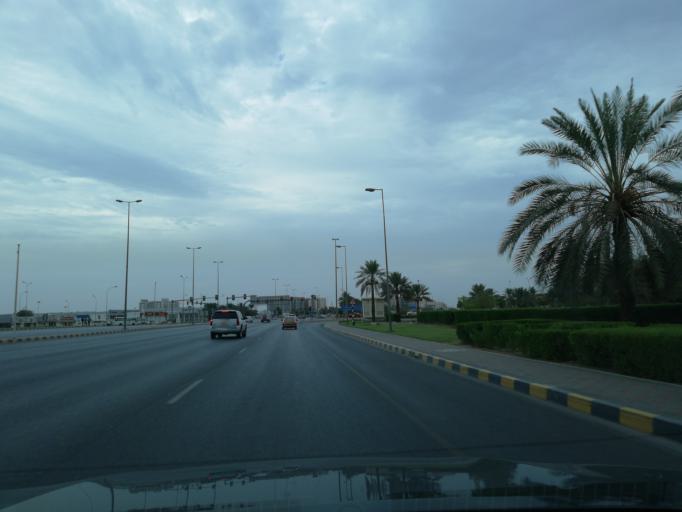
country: OM
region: Muhafazat Masqat
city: Bawshar
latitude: 23.5808
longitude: 58.3816
